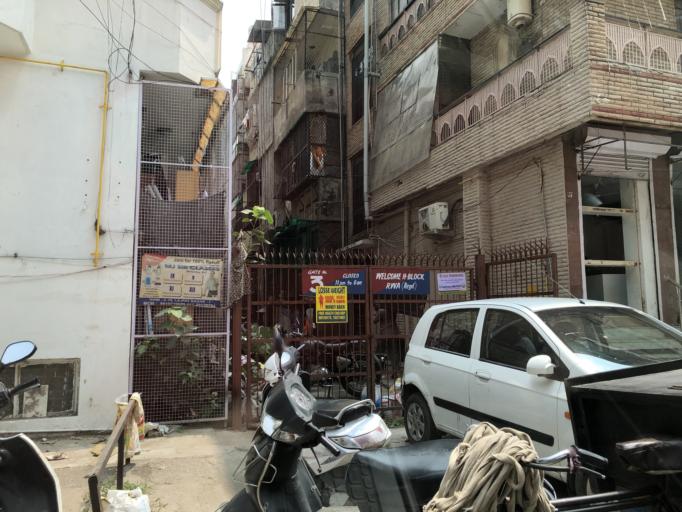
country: IN
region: NCT
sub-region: New Delhi
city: New Delhi
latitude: 28.5772
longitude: 77.2432
